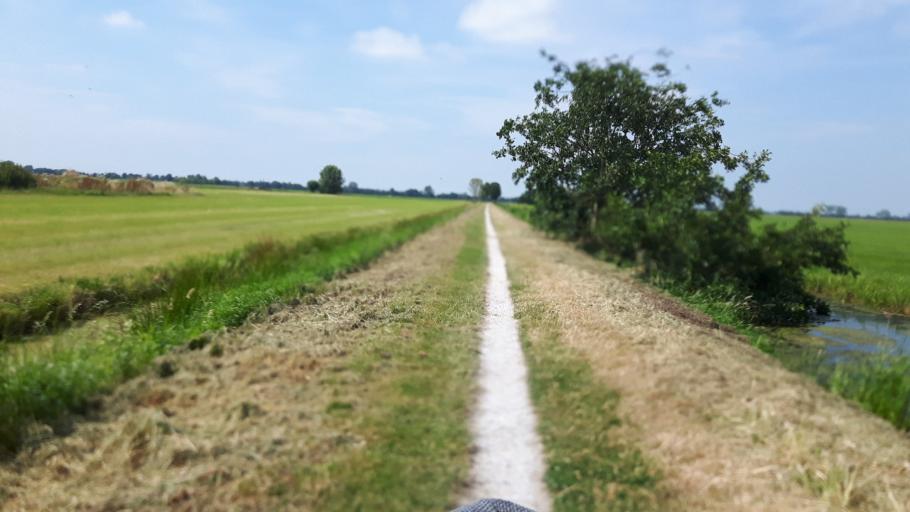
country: NL
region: Utrecht
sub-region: Gemeente Lopik
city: Lopik
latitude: 51.9678
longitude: 4.8979
